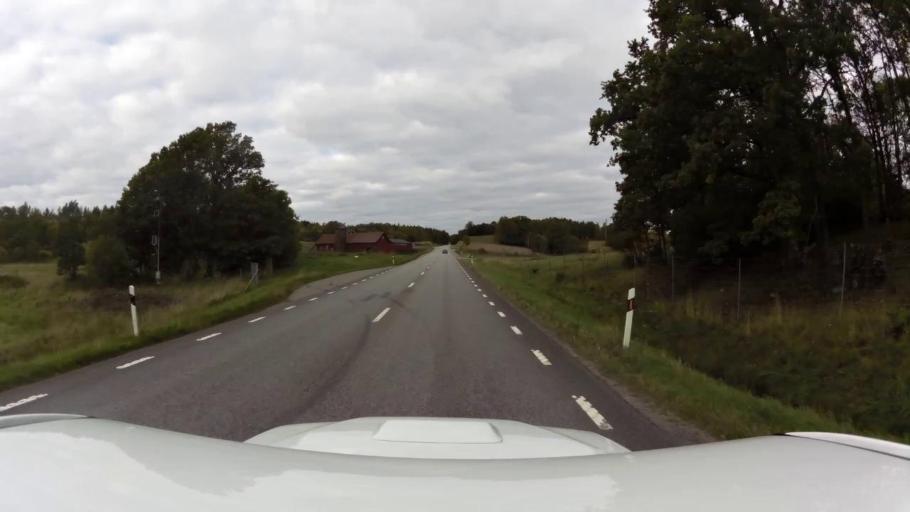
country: SE
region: OEstergoetland
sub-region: Kinda Kommun
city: Rimforsa
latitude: 58.2337
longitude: 15.6339
